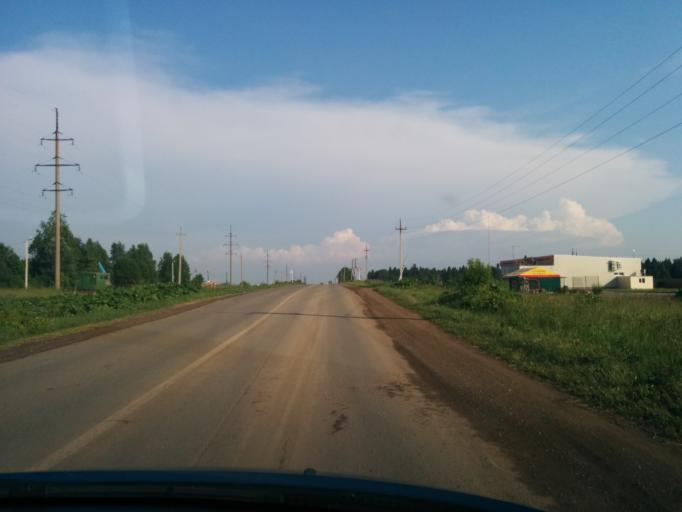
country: RU
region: Perm
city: Polazna
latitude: 58.2284
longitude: 56.2908
